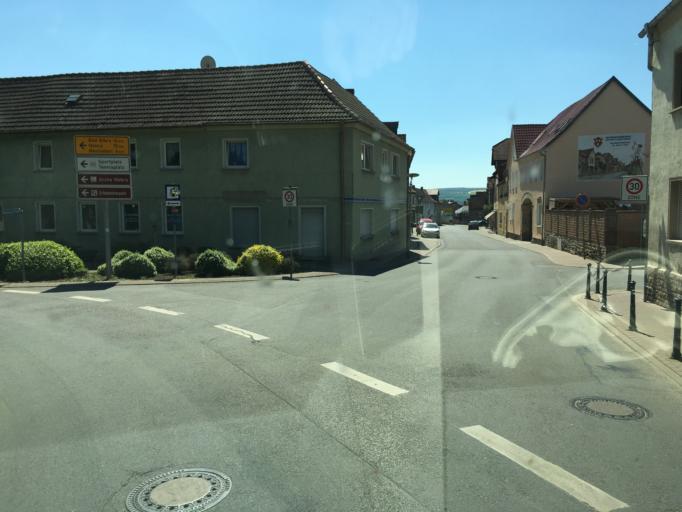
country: DE
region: Thuringia
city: Rossleben
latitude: 51.2967
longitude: 11.4328
